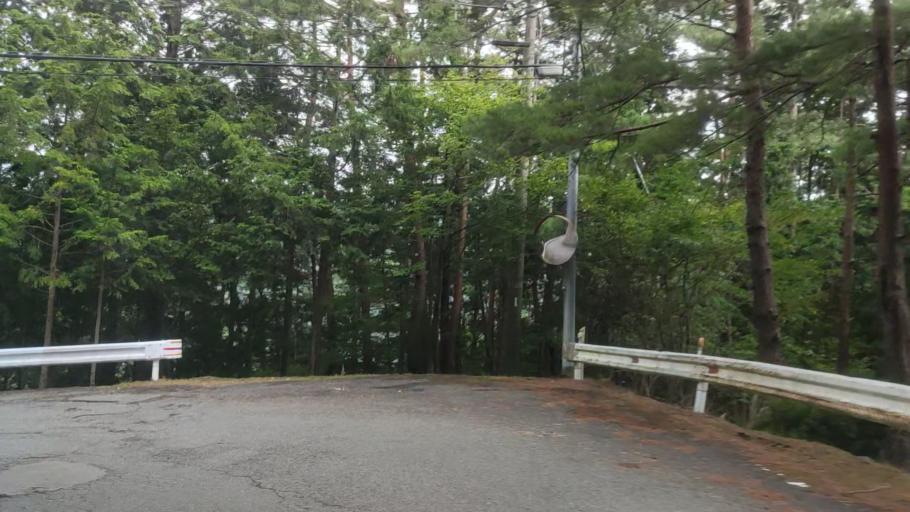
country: JP
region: Wakayama
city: Koya
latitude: 34.2231
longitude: 135.6172
